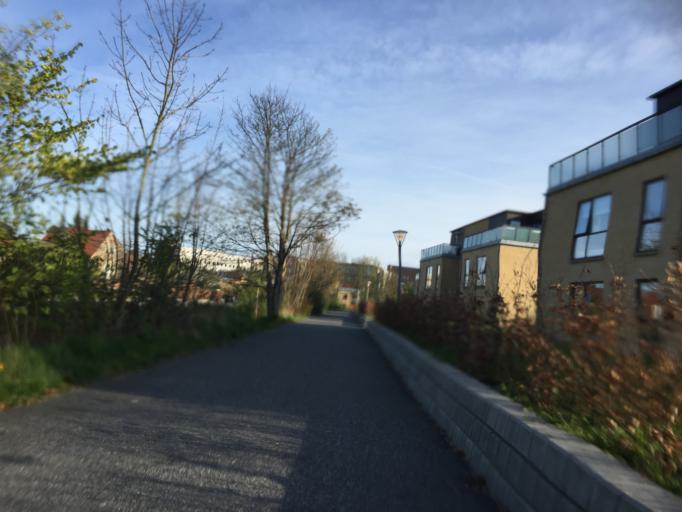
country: DK
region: Capital Region
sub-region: Frederiksberg Kommune
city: Frederiksberg
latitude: 55.7253
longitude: 12.5400
